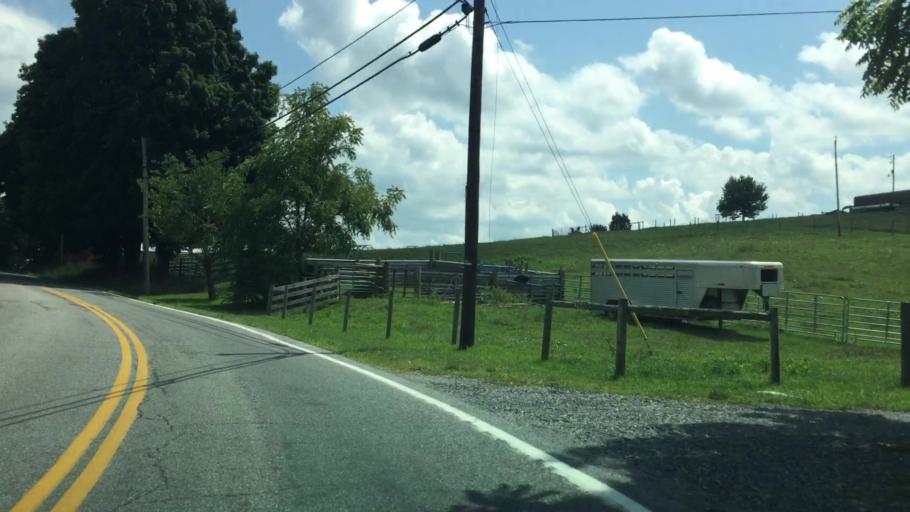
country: US
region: Virginia
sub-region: Pulaski County
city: Pulaski
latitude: 37.0096
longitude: -80.7440
